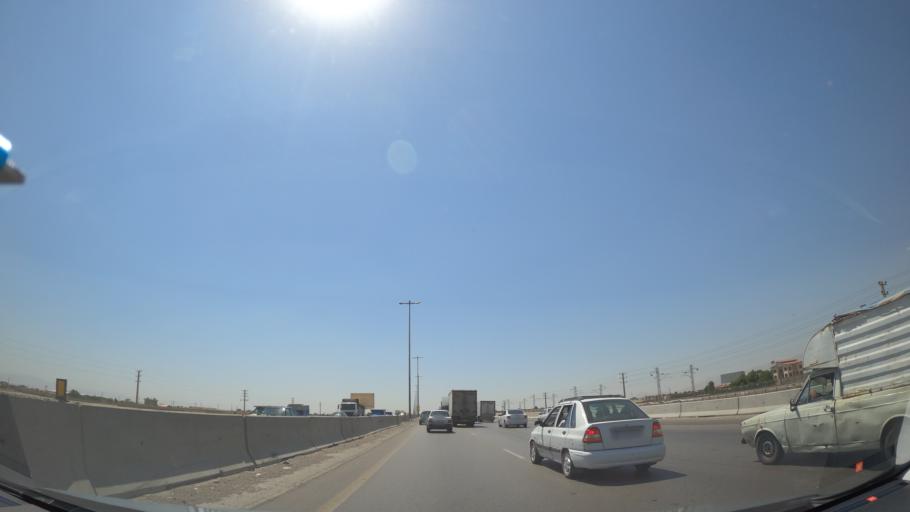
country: IR
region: Alborz
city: Hashtgerd
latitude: 35.9152
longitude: 50.8074
